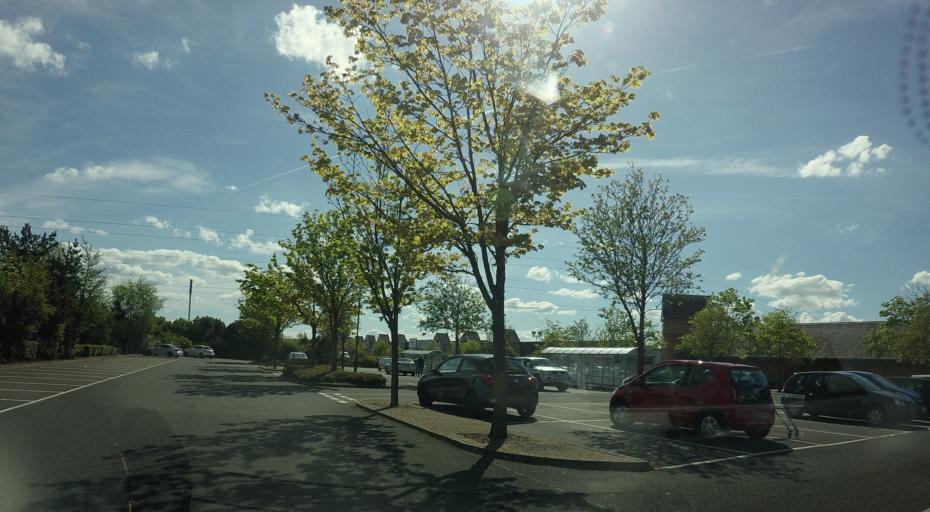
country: GB
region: Scotland
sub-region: Stirling
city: Bannockburn
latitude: 56.1158
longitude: -3.9088
